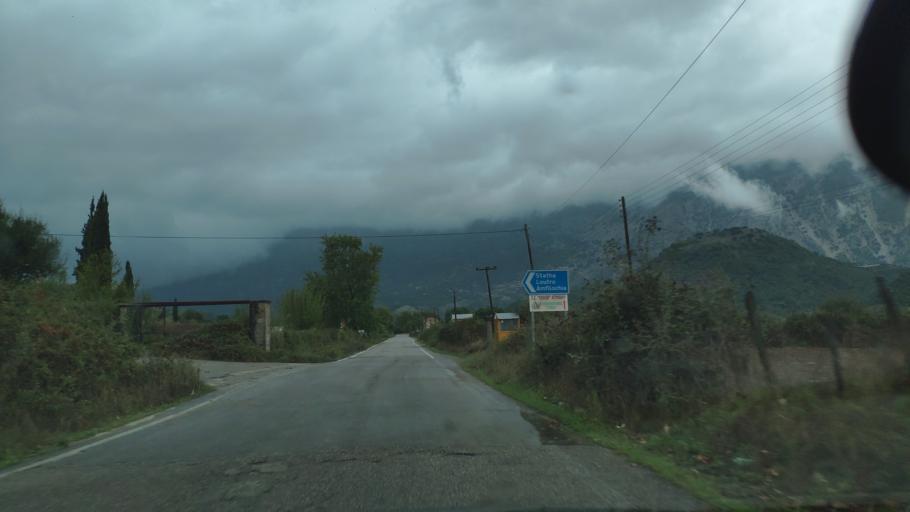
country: GR
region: West Greece
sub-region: Nomos Aitolias kai Akarnanias
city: Krikellos
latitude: 39.0067
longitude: 21.3093
